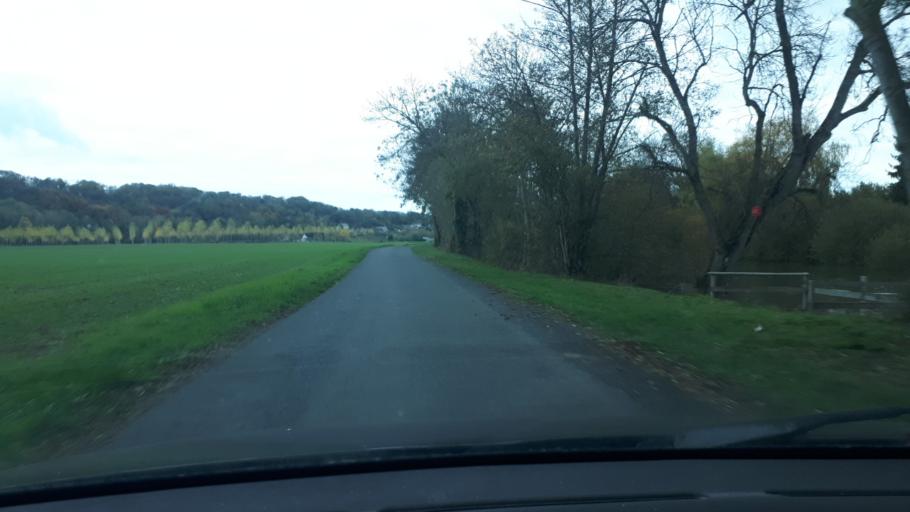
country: FR
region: Centre
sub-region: Departement du Loir-et-Cher
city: Lunay
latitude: 47.7681
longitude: 0.9431
